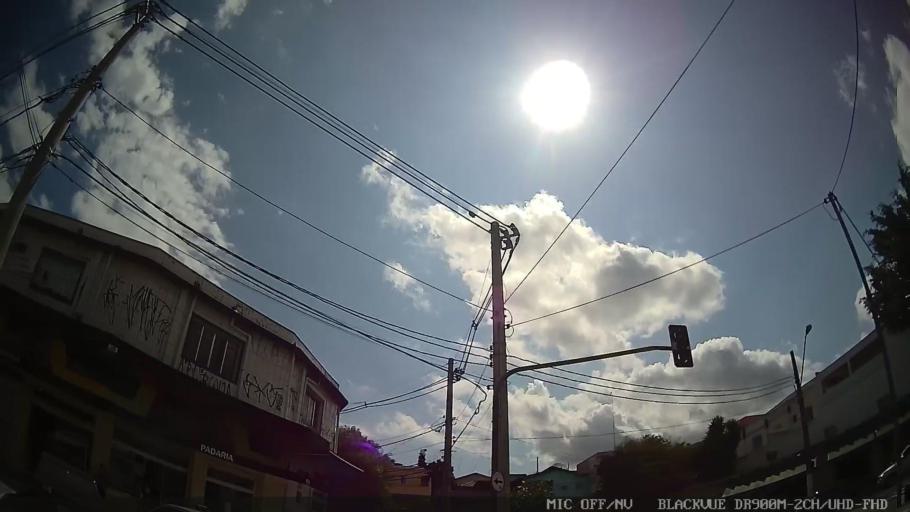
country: BR
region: Sao Paulo
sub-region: Guarulhos
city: Guarulhos
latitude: -23.4907
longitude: -46.4791
